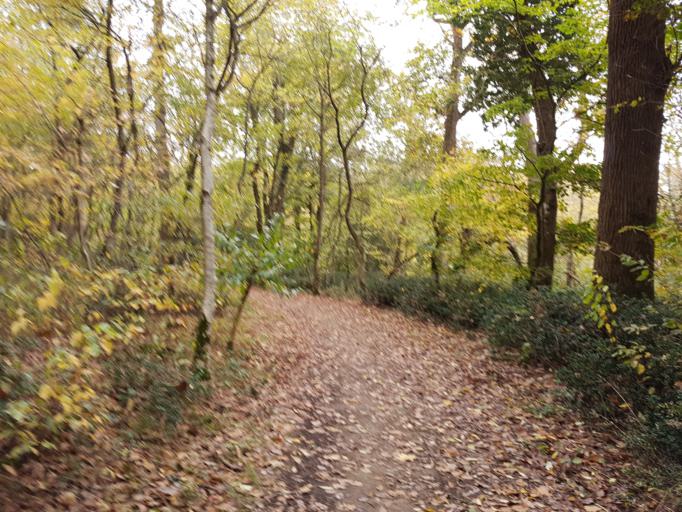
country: FR
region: Pays de la Loire
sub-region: Departement de Maine-et-Loire
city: Beaupreau
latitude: 47.1996
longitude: -0.9838
